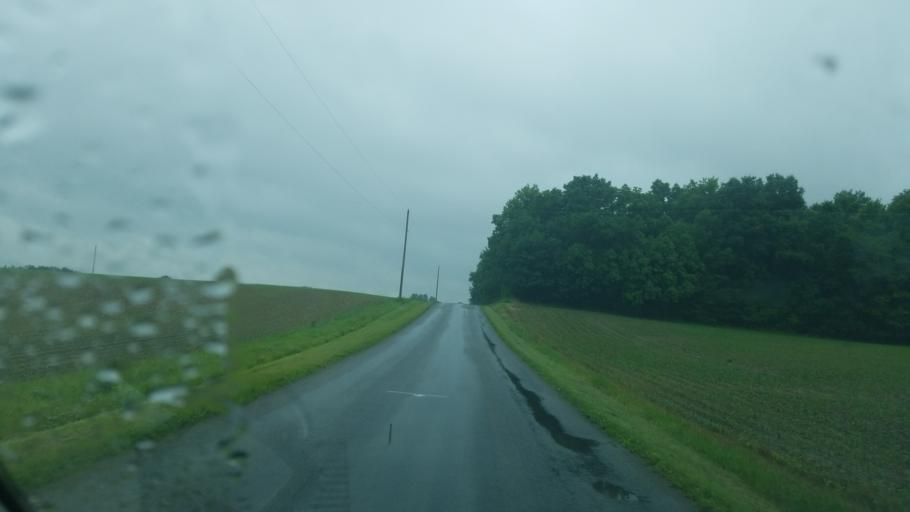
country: US
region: Ohio
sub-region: Richland County
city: Shelby
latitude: 40.9328
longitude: -82.5712
